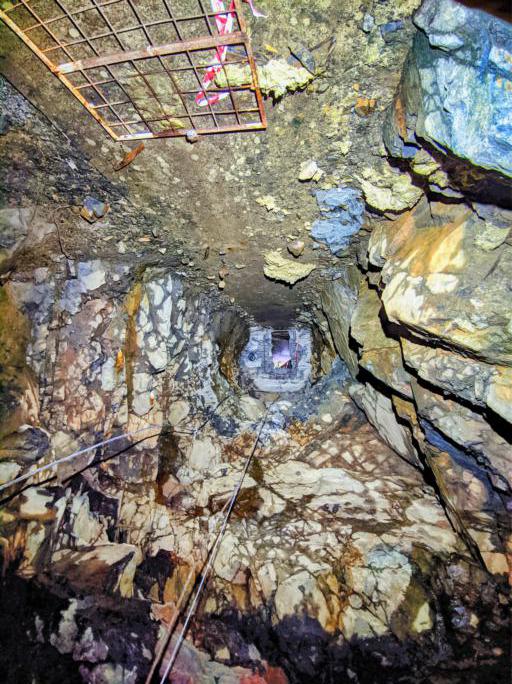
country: NO
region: Ostfold
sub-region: Trogstad
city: Skjonhaug
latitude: 59.6318
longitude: 11.3378
